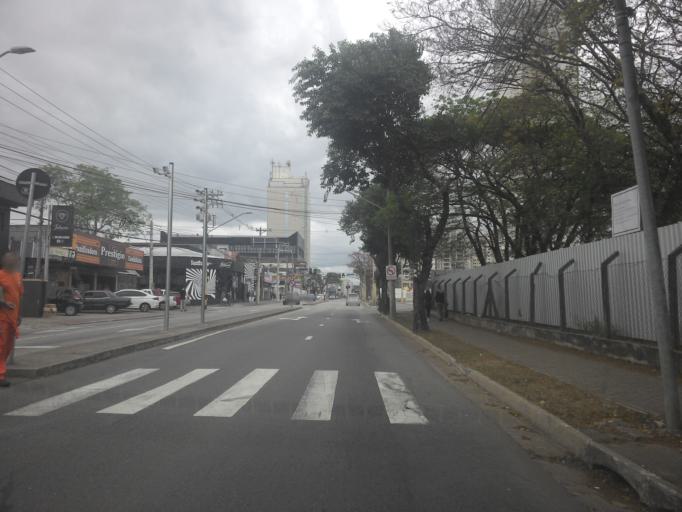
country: BR
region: Sao Paulo
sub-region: Sao Jose Dos Campos
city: Sao Jose dos Campos
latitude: -23.2264
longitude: -45.9121
